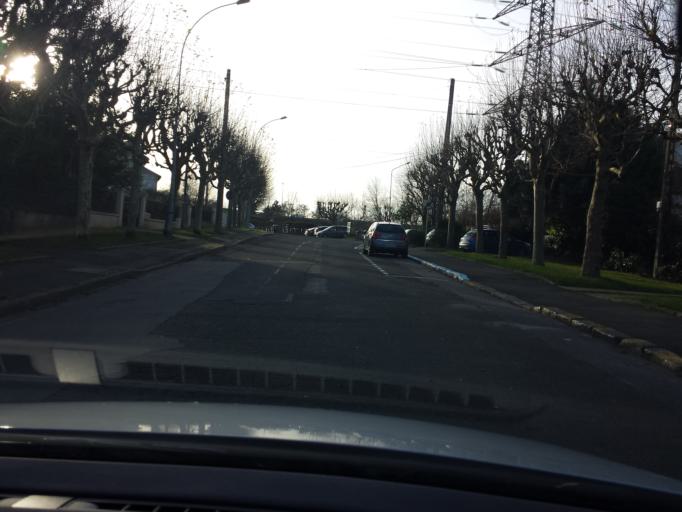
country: FR
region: Ile-de-France
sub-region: Departement de l'Essonne
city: Palaiseau
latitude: 48.7208
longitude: 2.2585
